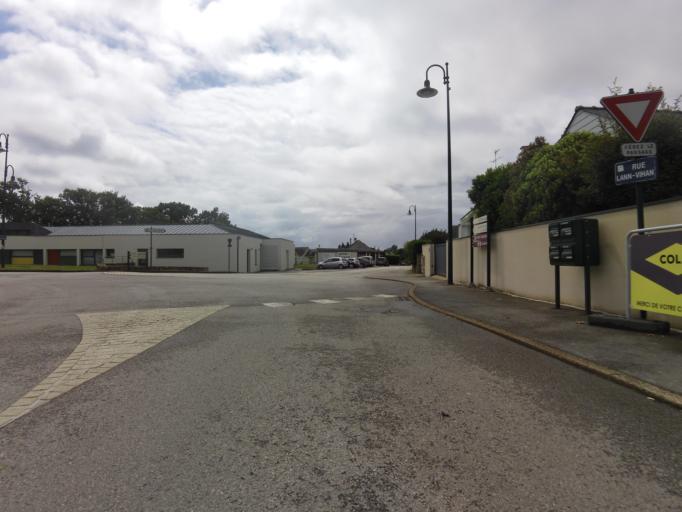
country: FR
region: Brittany
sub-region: Departement du Morbihan
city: Baden
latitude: 47.6178
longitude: -2.9200
